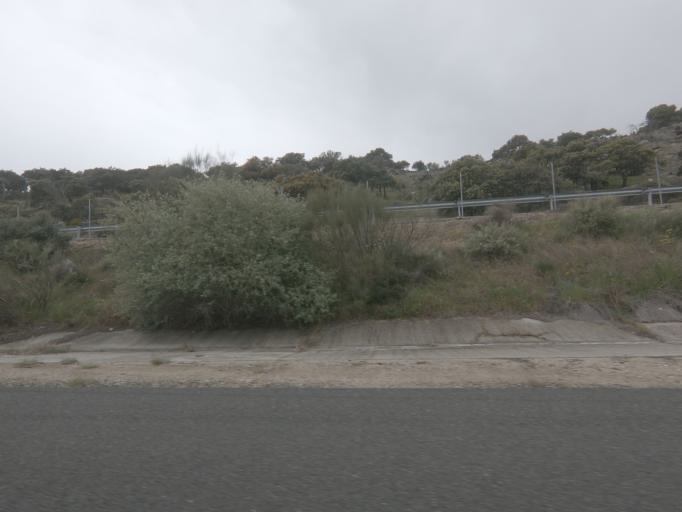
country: ES
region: Extremadura
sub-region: Provincia de Caceres
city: Villar de Plasencia
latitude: 40.1270
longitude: -6.0510
